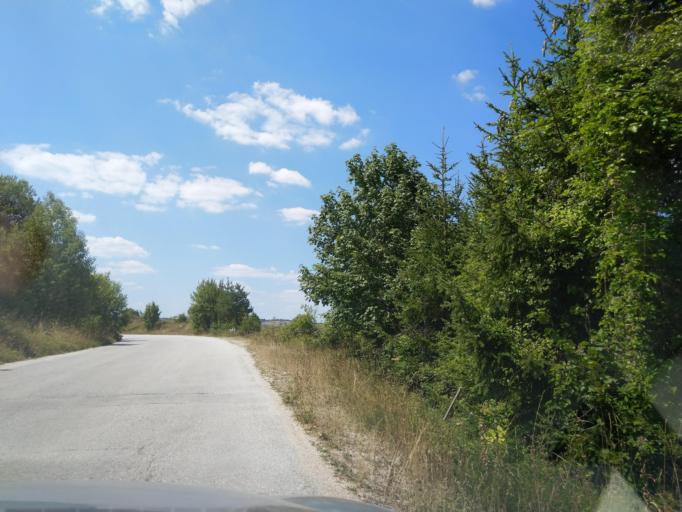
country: RS
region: Central Serbia
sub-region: Zlatiborski Okrug
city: Nova Varos
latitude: 43.4281
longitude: 19.9403
